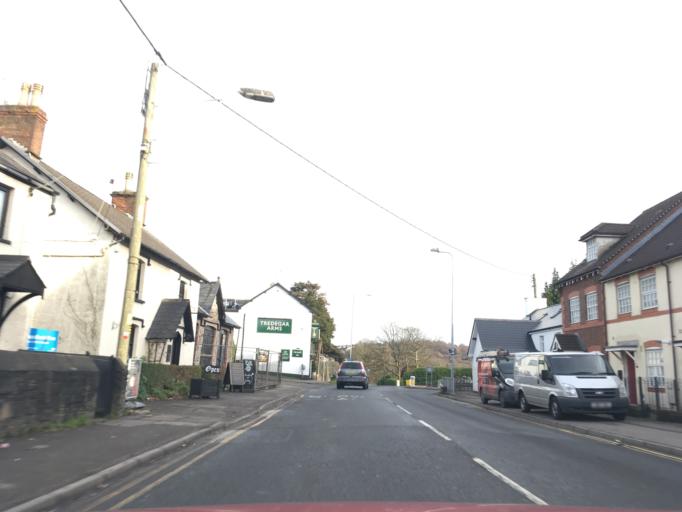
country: GB
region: Wales
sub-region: Newport
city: Newport
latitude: 51.5776
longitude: -3.0461
